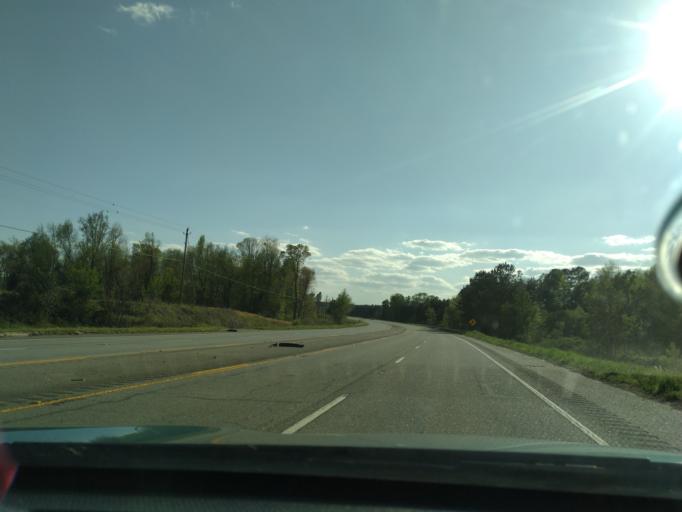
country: US
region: South Carolina
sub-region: Williamsburg County
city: Kingstree
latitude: 33.6347
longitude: -79.9168
